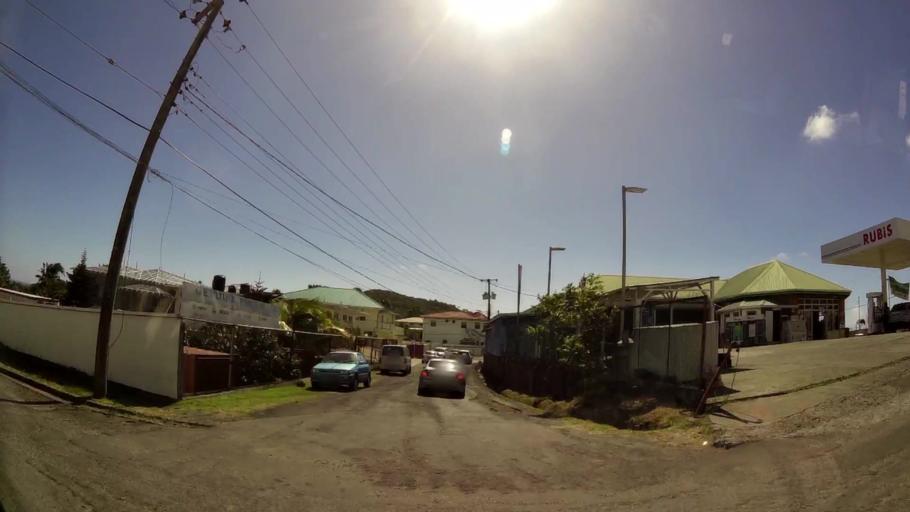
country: LC
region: Laborie Quarter
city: Laborie
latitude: 13.7503
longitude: -60.9701
